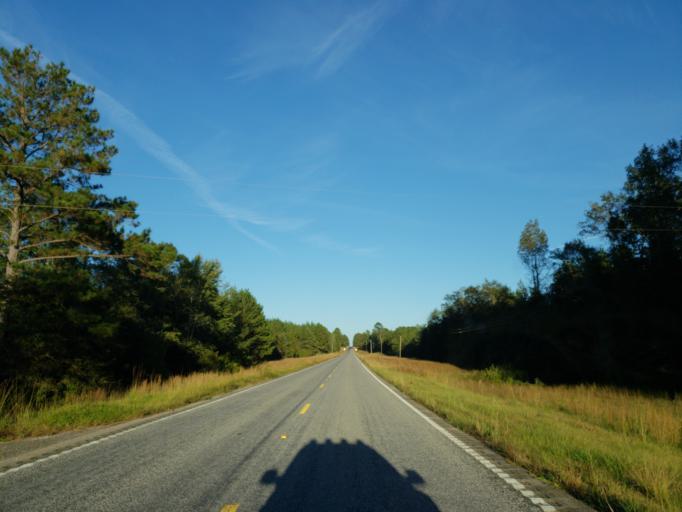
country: US
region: Mississippi
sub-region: Wayne County
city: Belmont
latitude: 31.4103
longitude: -88.6087
